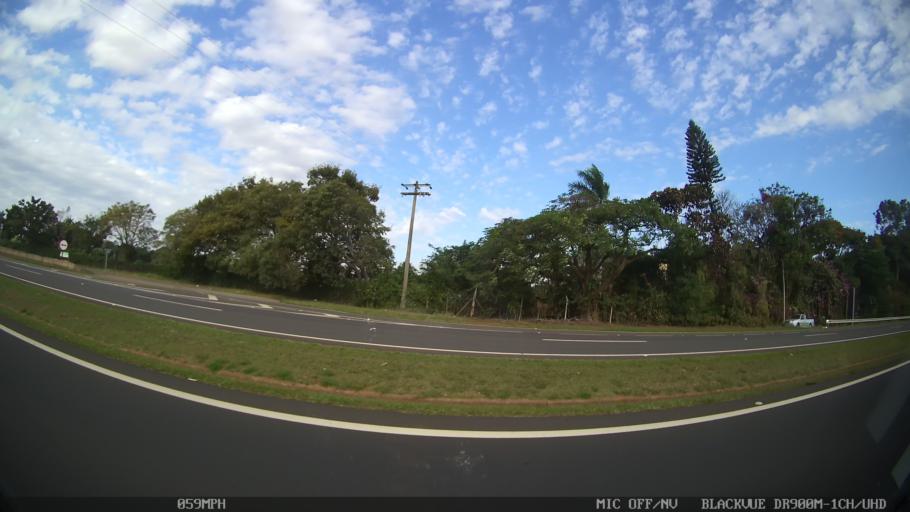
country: BR
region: Sao Paulo
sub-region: Iracemapolis
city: Iracemapolis
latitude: -22.5911
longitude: -47.4625
